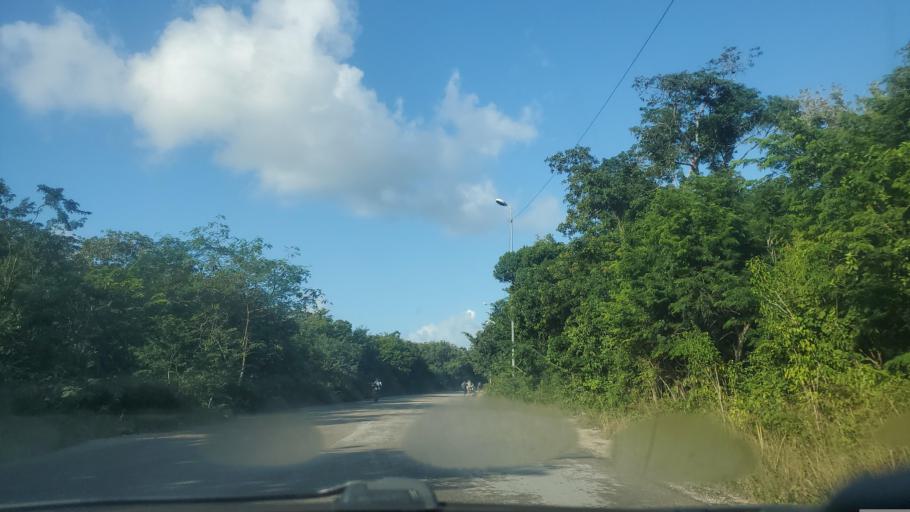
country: MX
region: Quintana Roo
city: Tulum
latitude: 20.2090
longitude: -87.4806
